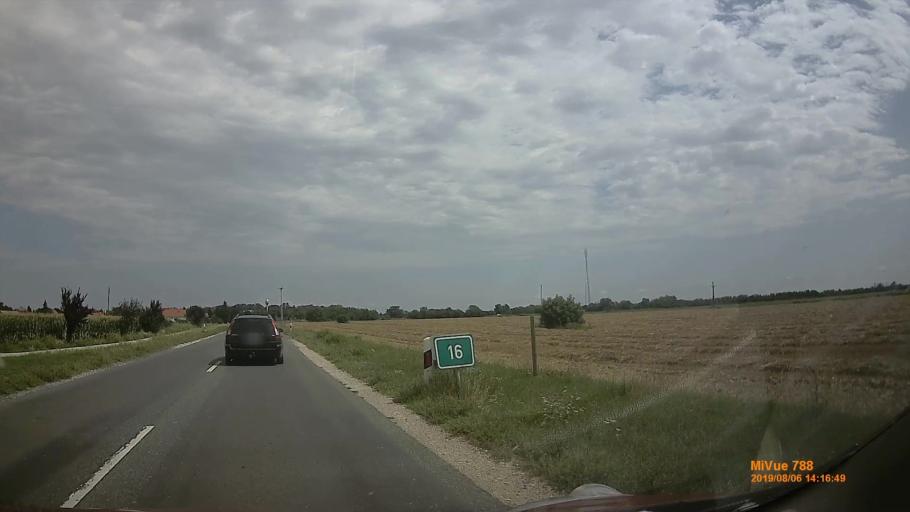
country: HU
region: Vas
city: Taplanszentkereszt
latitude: 47.1894
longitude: 16.7250
